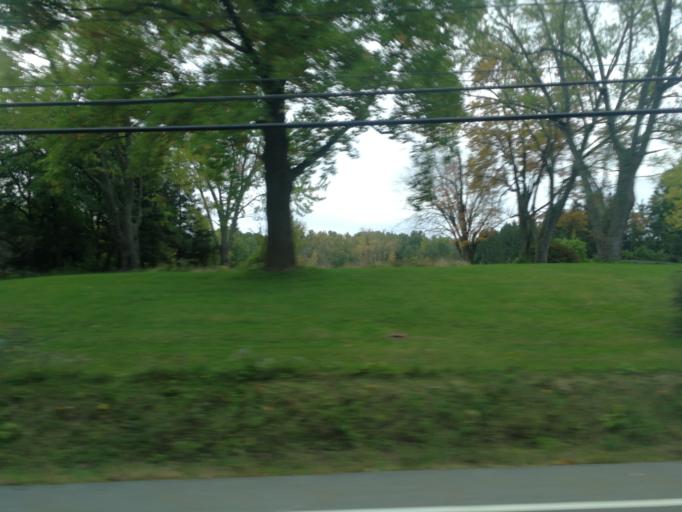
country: US
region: New York
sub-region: Saratoga County
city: Country Knolls
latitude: 42.9715
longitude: -73.7886
